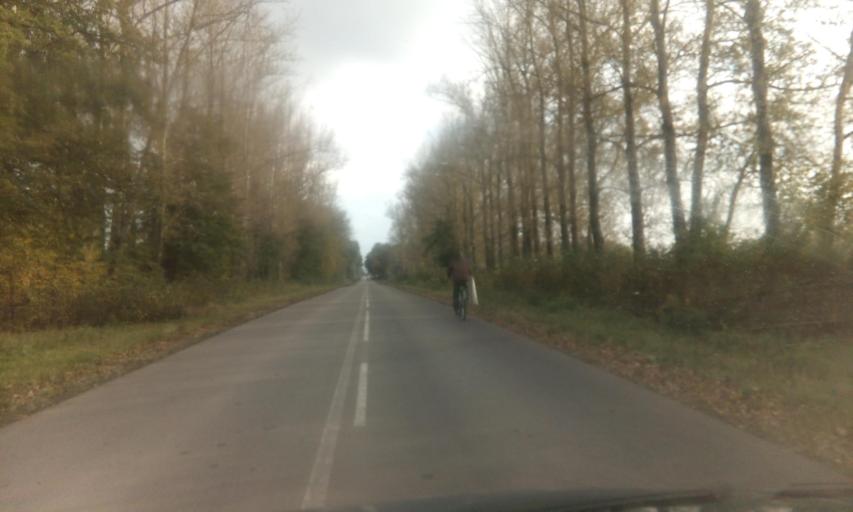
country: RU
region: Tula
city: Partizan
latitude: 53.9559
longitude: 38.0964
